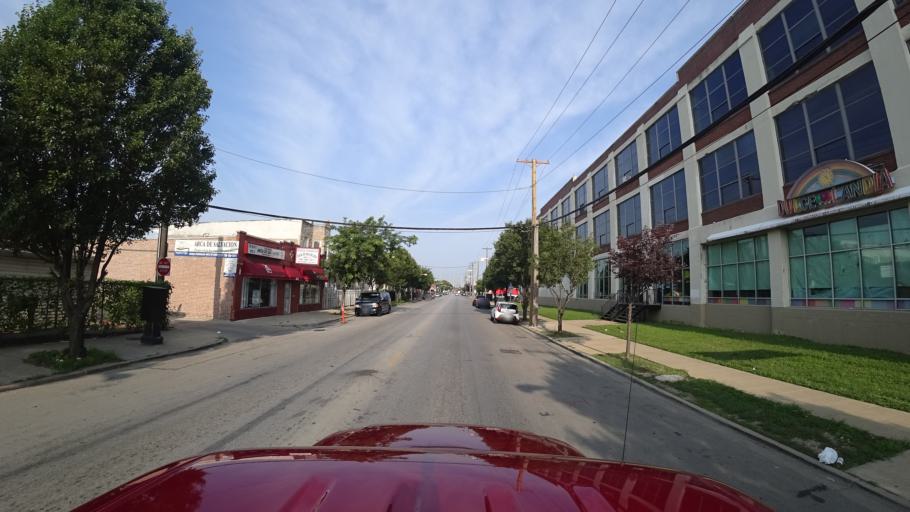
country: US
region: Illinois
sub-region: Cook County
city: Chicago
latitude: 41.8302
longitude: -87.6903
